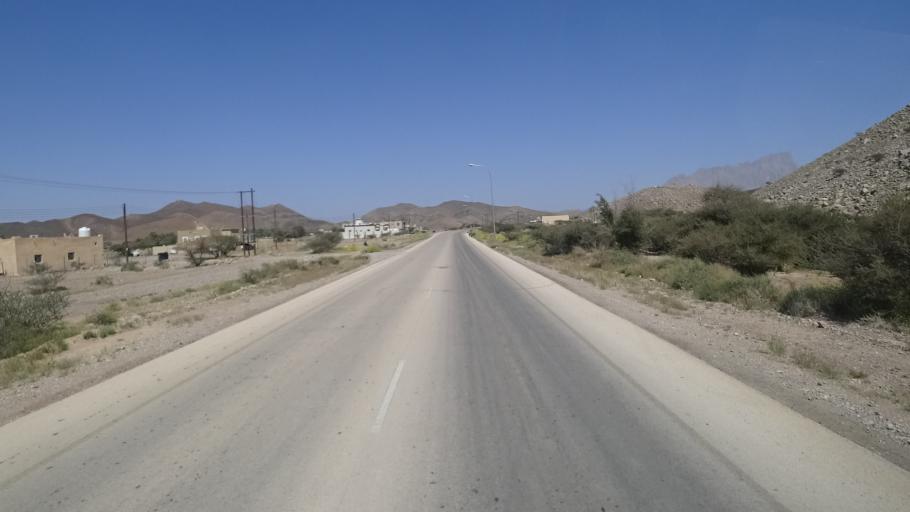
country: OM
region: Az Zahirah
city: `Ibri
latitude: 23.1764
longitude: 56.9187
